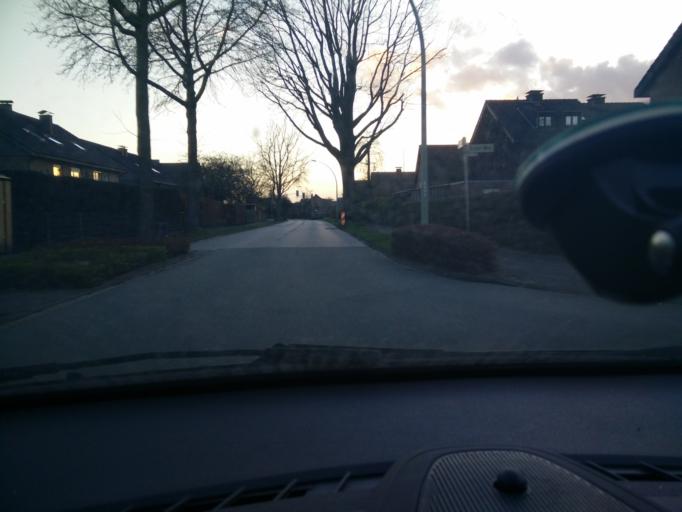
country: DE
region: North Rhine-Westphalia
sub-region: Regierungsbezirk Munster
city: Raesfeld
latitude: 51.7710
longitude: 6.8353
